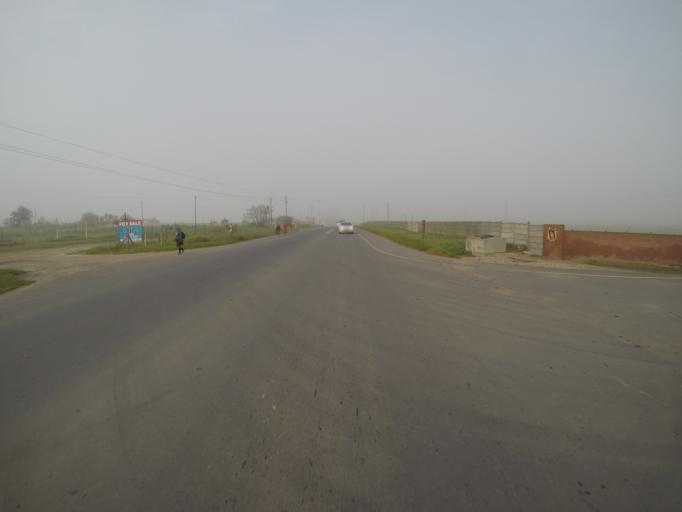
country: ZA
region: Western Cape
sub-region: City of Cape Town
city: Kraaifontein
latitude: -33.7877
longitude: 18.7007
